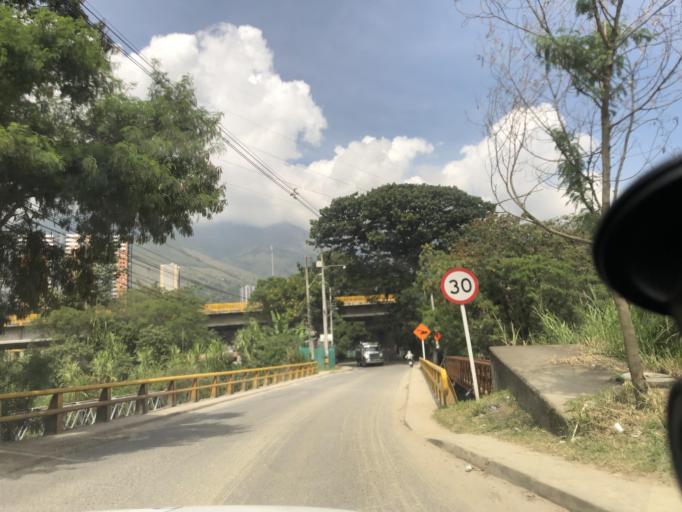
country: CO
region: Antioquia
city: Bello
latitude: 6.3355
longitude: -75.5376
